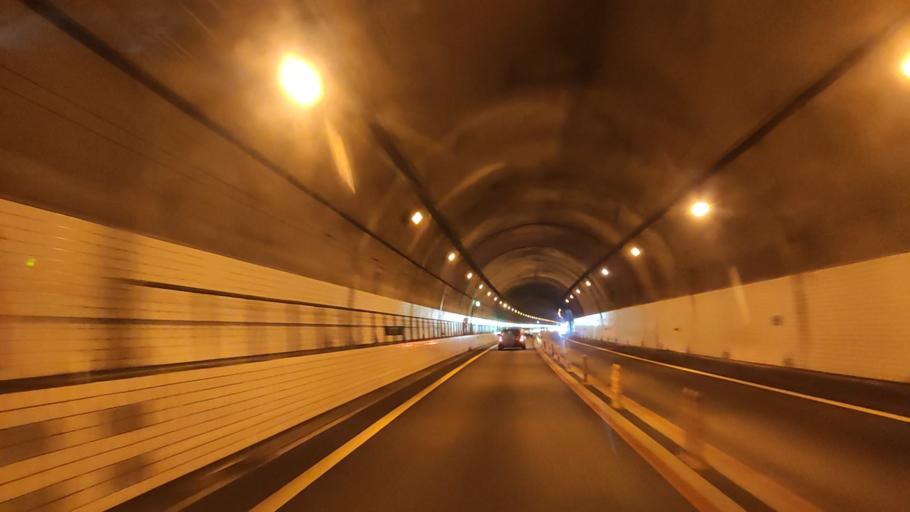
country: JP
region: Tokushima
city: Ikedacho
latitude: 34.0207
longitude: 133.8082
